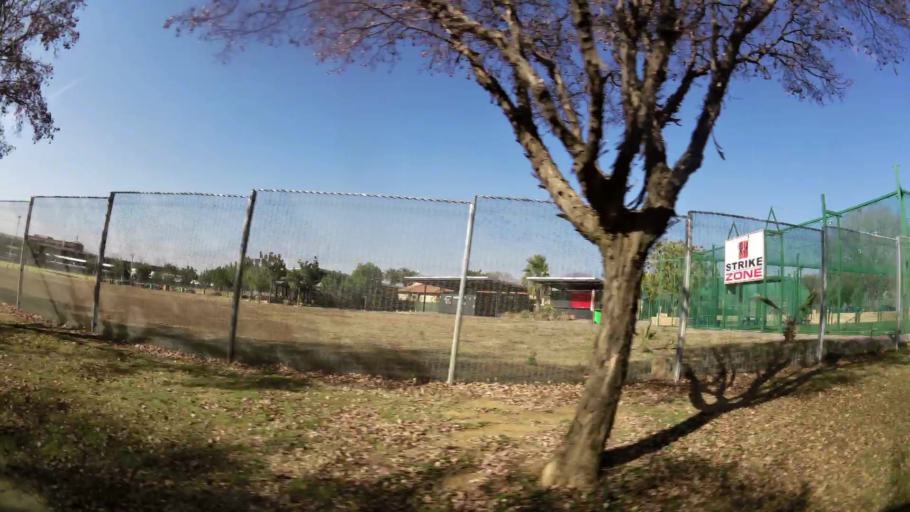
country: ZA
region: Gauteng
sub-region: City of Tshwane Metropolitan Municipality
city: Pretoria
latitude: -25.7224
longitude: 28.2446
